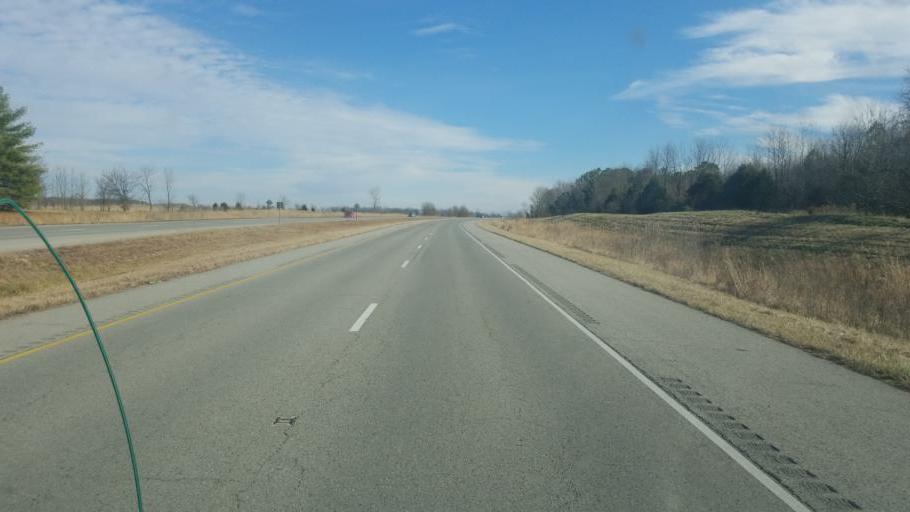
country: US
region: Illinois
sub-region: Williamson County
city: Marion
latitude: 37.7326
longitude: -88.7977
